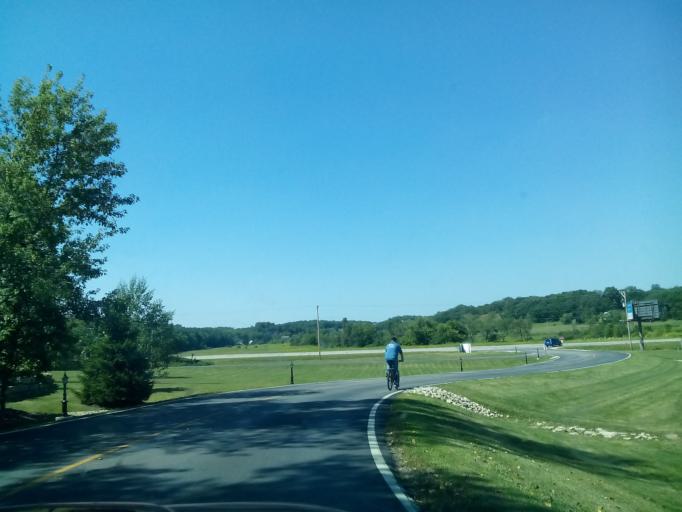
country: US
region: Wisconsin
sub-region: Green County
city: New Glarus
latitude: 42.7970
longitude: -89.6307
